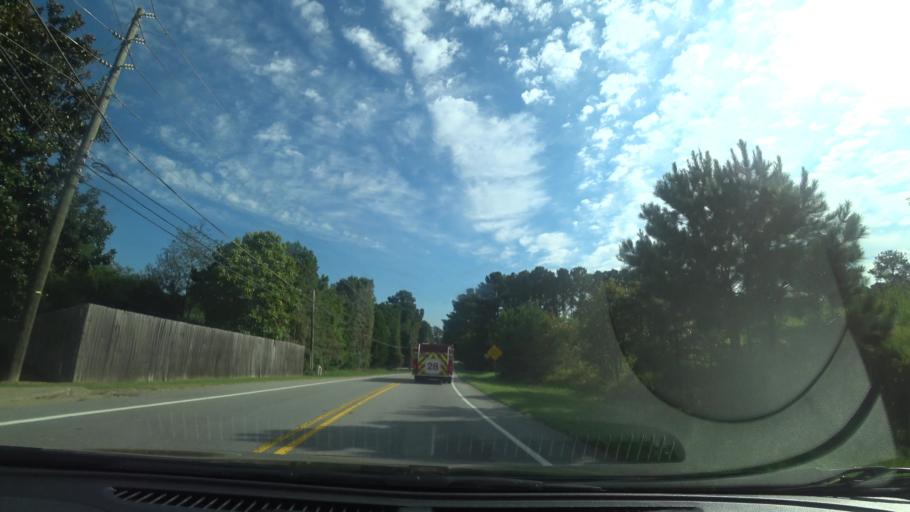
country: US
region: Georgia
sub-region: Gwinnett County
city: Grayson
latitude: 33.8486
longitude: -83.9574
